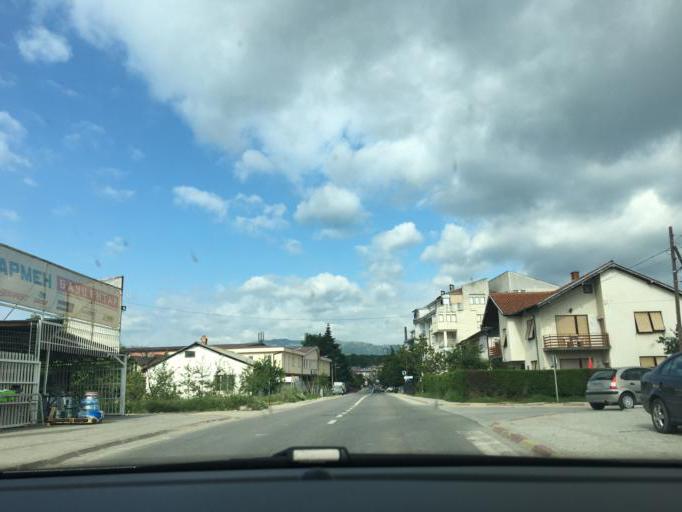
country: MK
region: Resen
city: Resen
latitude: 41.0855
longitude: 21.0153
